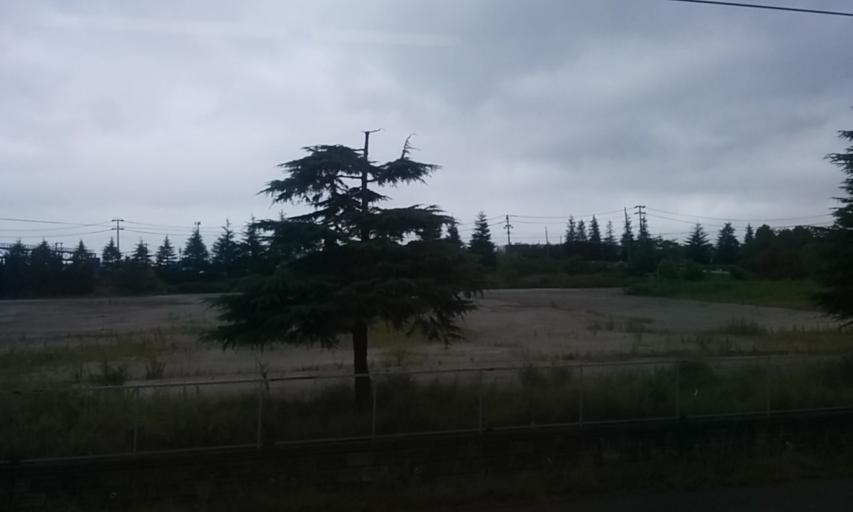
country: JP
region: Miyagi
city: Rifu
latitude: 38.2741
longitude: 140.9447
